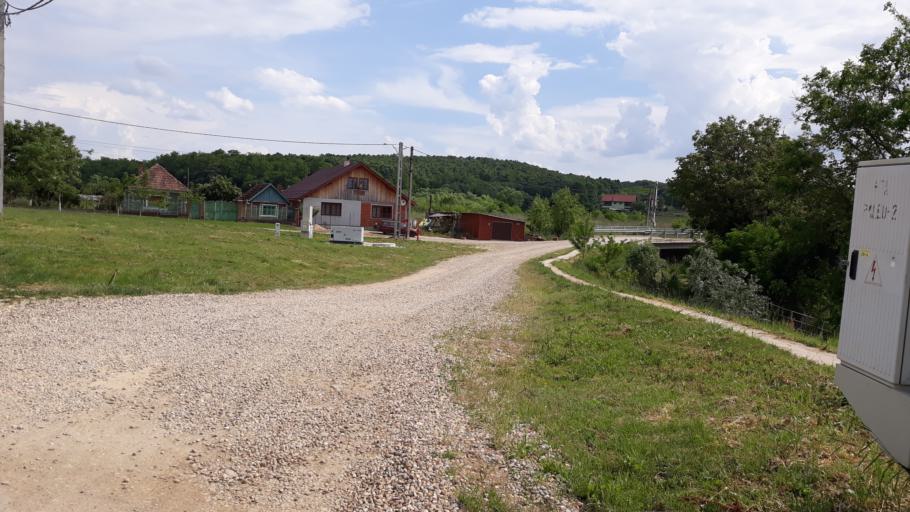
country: RO
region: Bihor
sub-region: Comuna Paleu
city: Paleu
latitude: 47.1123
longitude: 21.9530
